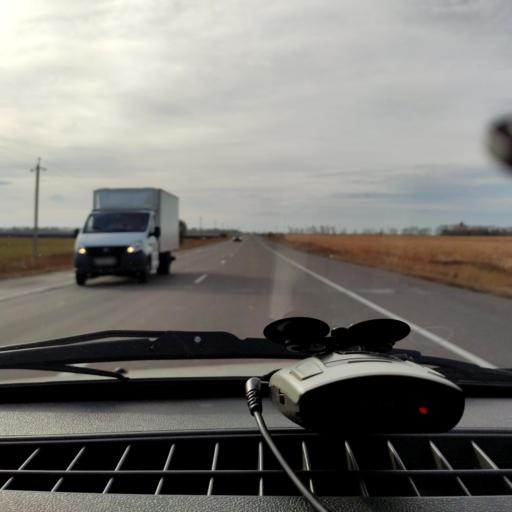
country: RU
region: Voronezj
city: Strelitsa
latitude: 51.5603
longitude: 38.9728
